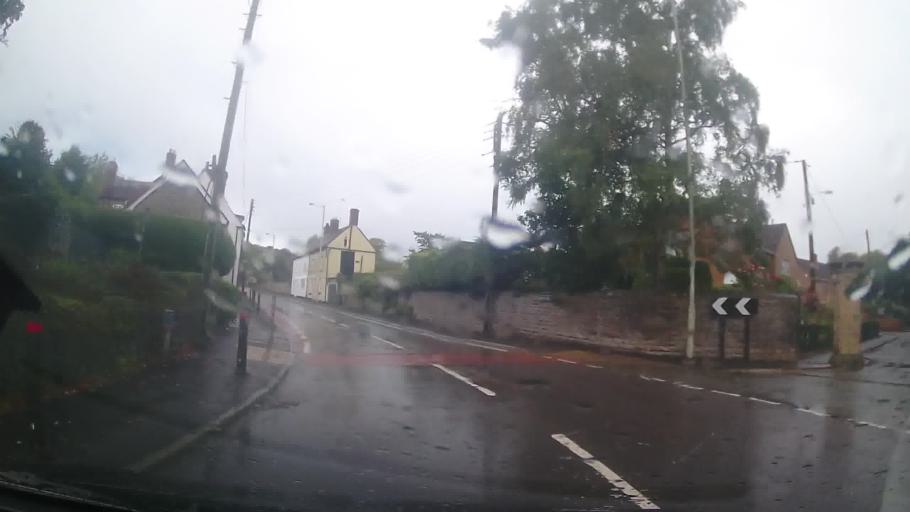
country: GB
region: England
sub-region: Shropshire
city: Much Wenlock
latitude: 52.5983
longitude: -2.5589
